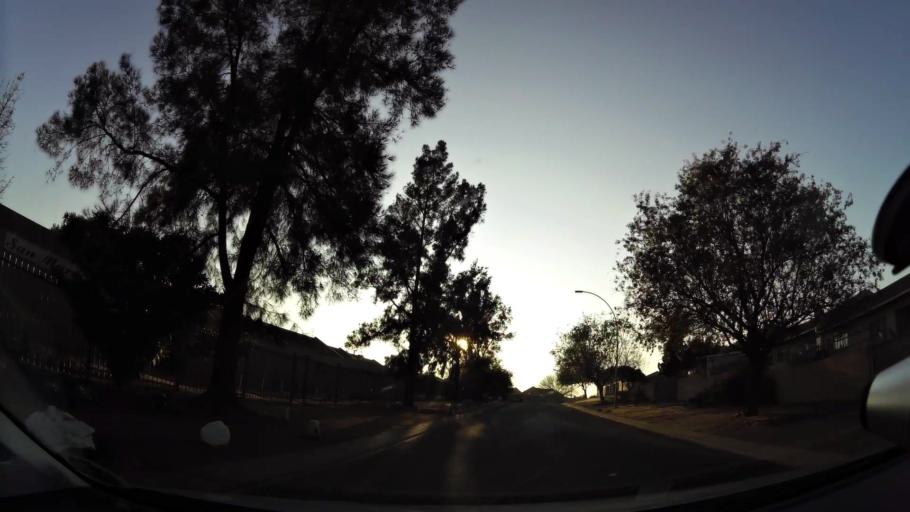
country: ZA
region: Orange Free State
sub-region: Mangaung Metropolitan Municipality
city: Bloemfontein
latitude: -29.0959
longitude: 26.1563
